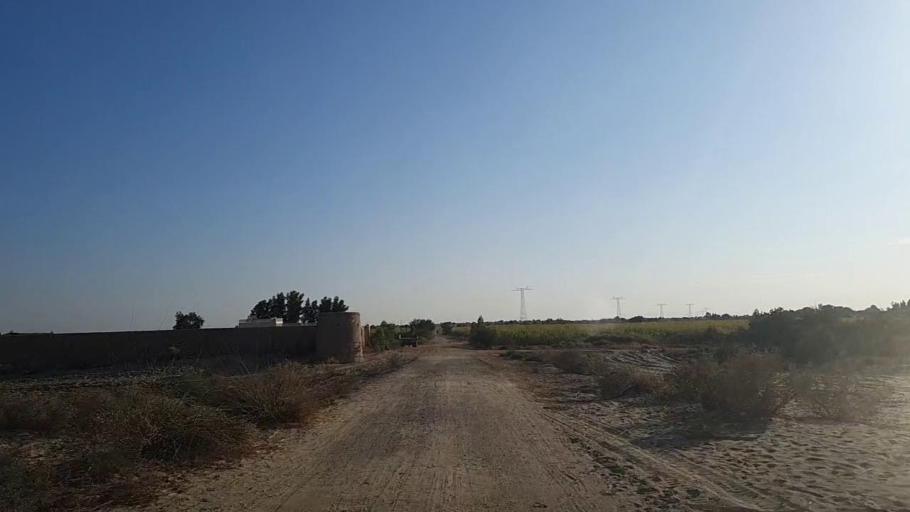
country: PK
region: Sindh
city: Khadro
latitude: 26.2708
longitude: 68.8603
